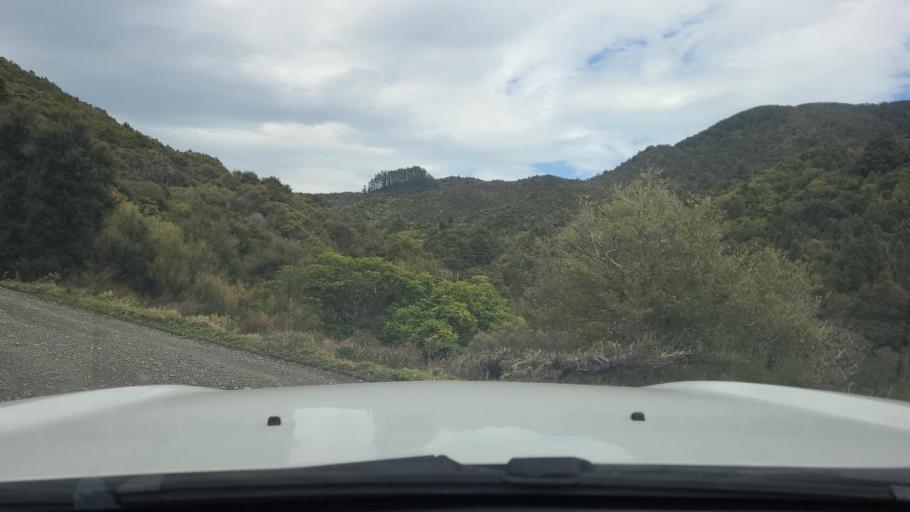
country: NZ
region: Wellington
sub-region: South Wairarapa District
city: Waipawa
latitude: -41.4078
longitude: 175.3636
